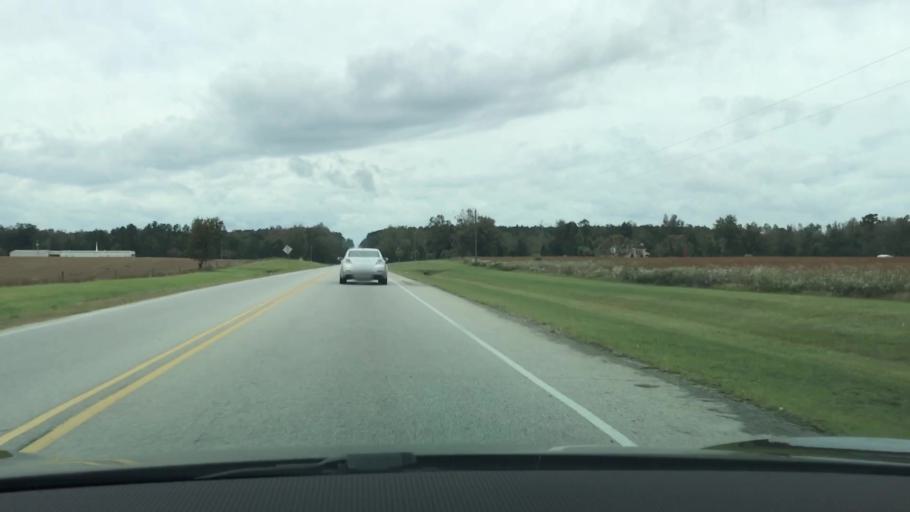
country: US
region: Georgia
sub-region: Jefferson County
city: Louisville
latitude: 32.9481
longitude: -82.3948
